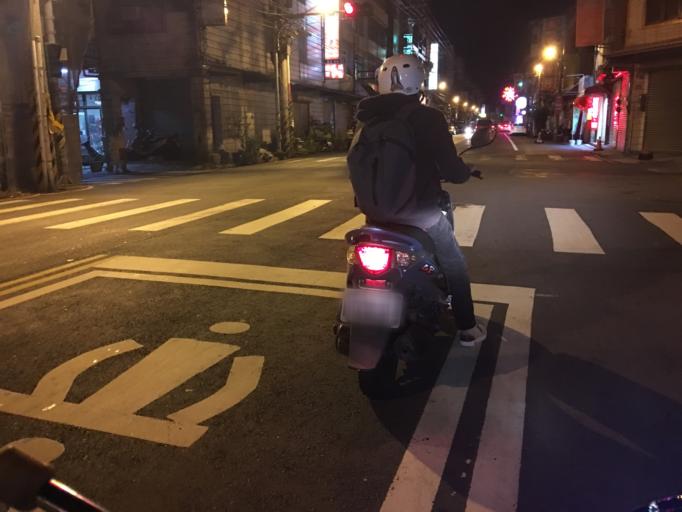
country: TW
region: Taiwan
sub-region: Hsinchu
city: Zhubei
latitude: 24.8422
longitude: 120.9981
